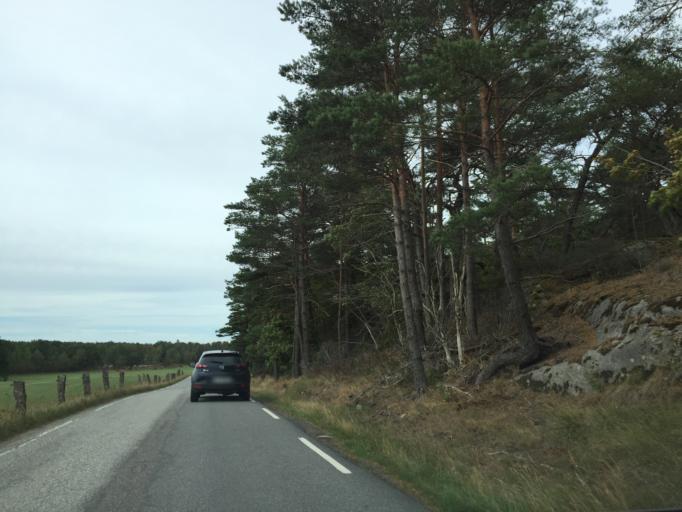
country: NO
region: Ostfold
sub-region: Hvaler
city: Skjaerhalden
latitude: 59.0334
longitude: 11.0249
